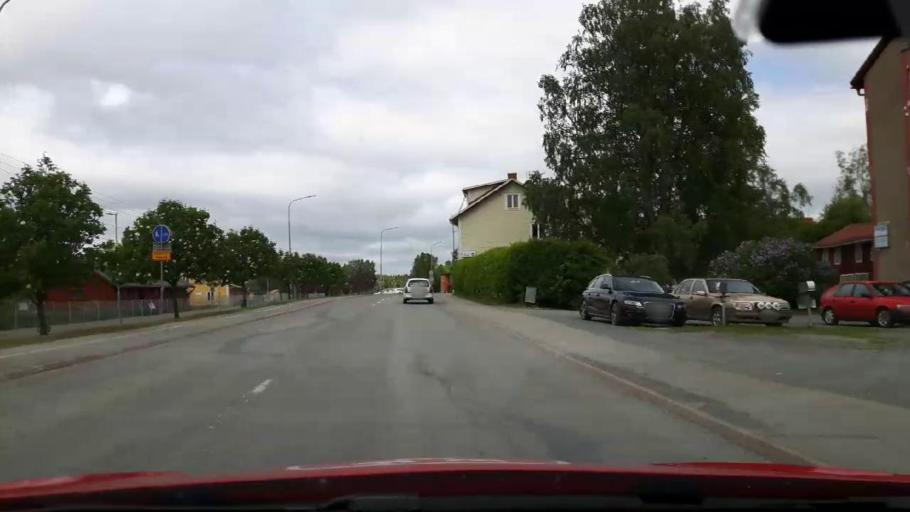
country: SE
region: Jaemtland
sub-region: Krokoms Kommun
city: Krokom
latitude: 63.3252
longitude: 14.4496
